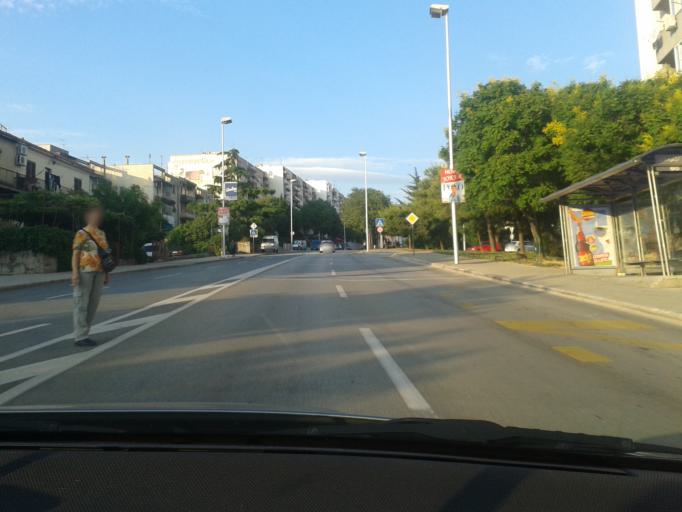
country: HR
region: Splitsko-Dalmatinska
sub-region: Grad Split
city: Split
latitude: 43.5159
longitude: 16.4526
